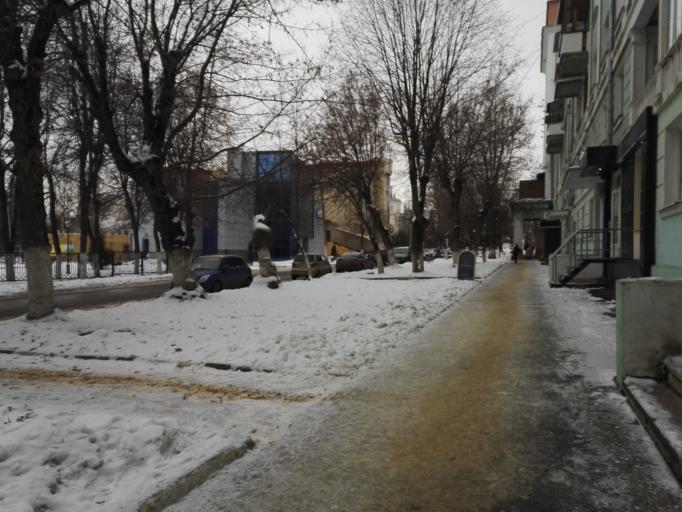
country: RU
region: Tula
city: Novomoskovsk
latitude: 54.0114
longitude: 38.2998
